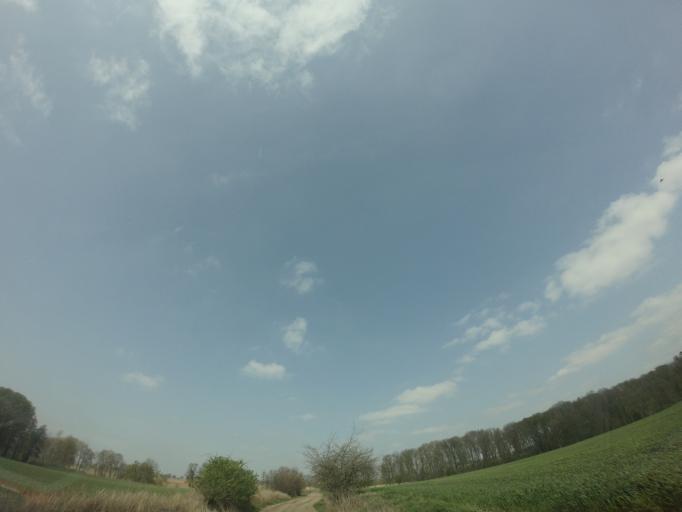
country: PL
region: West Pomeranian Voivodeship
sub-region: Powiat choszczenski
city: Pelczyce
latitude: 53.0936
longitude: 15.3397
